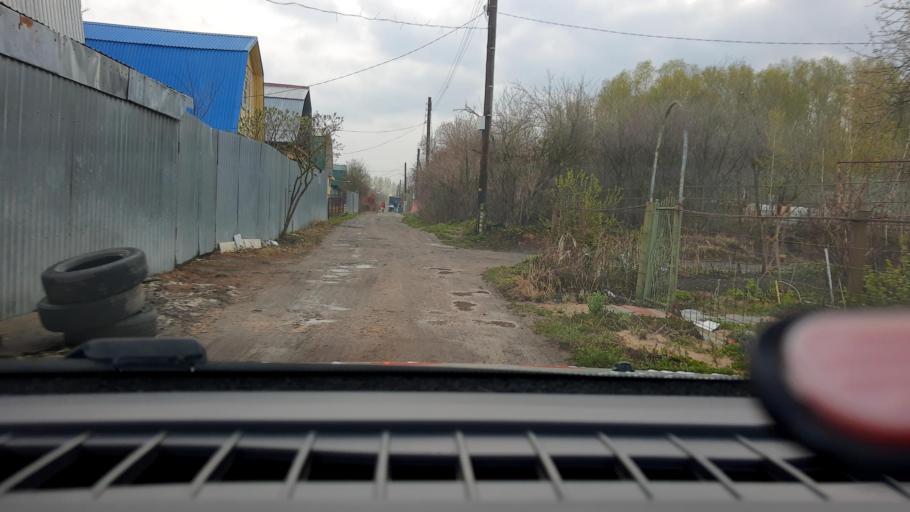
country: RU
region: Nizjnij Novgorod
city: Gorbatovka
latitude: 56.2993
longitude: 43.7688
